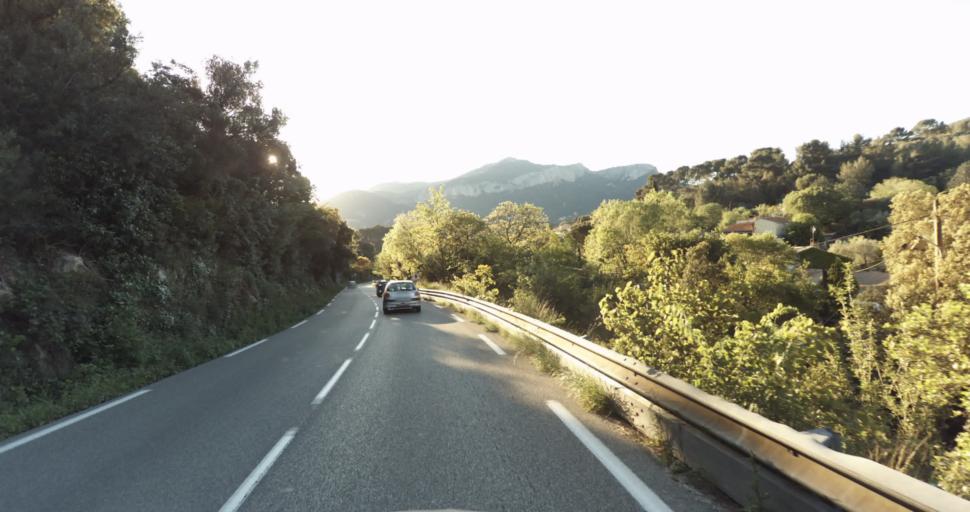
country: FR
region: Provence-Alpes-Cote d'Azur
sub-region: Departement du Var
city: Le Revest-les-Eaux
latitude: 43.1643
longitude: 5.9417
